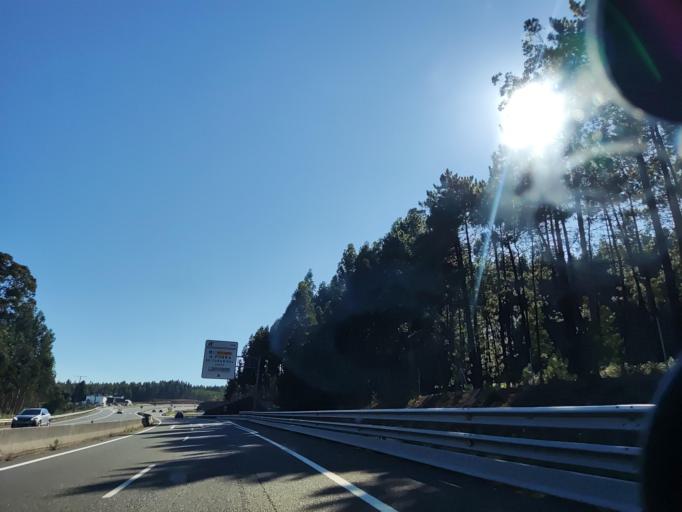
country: ES
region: Galicia
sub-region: Provincia da Coruna
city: Boiro
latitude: 42.6110
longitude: -8.9616
